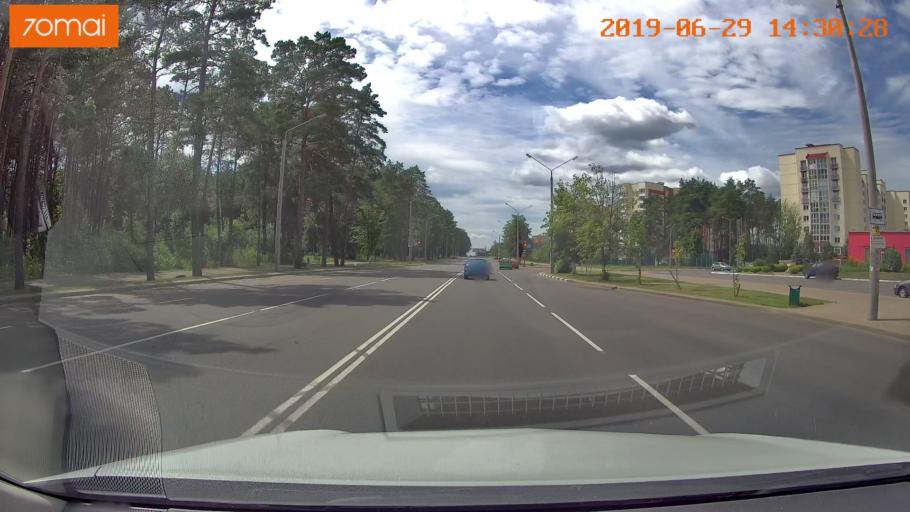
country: BY
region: Minsk
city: Salihorsk
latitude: 52.7814
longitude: 27.5173
